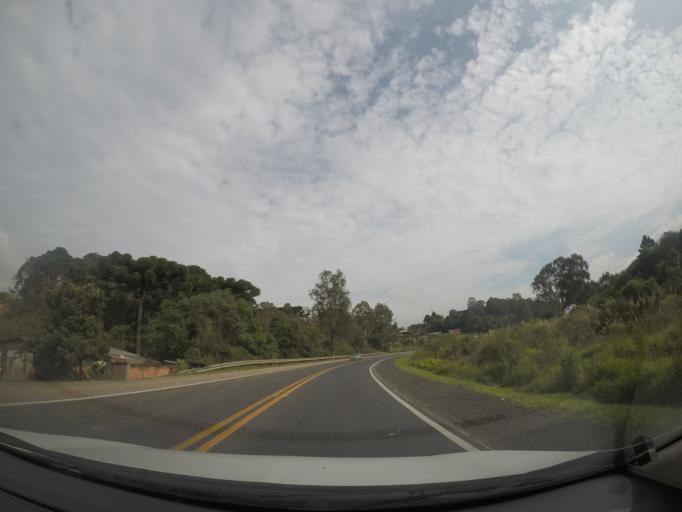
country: BR
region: Parana
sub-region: Colombo
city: Colombo
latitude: -25.3417
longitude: -49.2395
